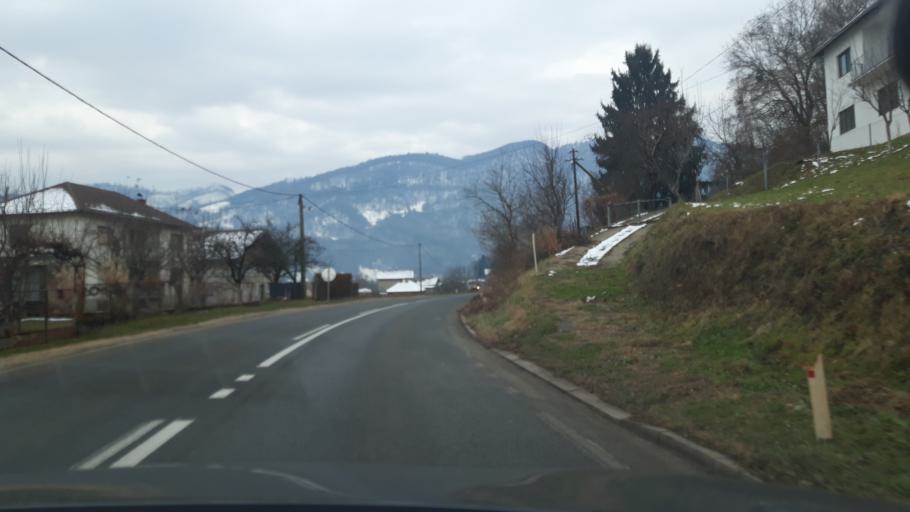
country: RS
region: Central Serbia
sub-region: Macvanski Okrug
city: Mali Zvornik
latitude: 44.2934
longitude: 19.1496
